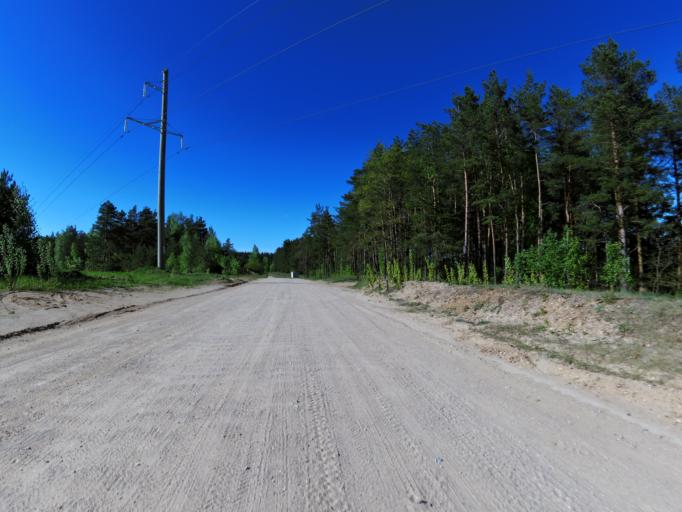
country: LT
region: Vilnius County
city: Pilaite
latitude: 54.6925
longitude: 25.1581
